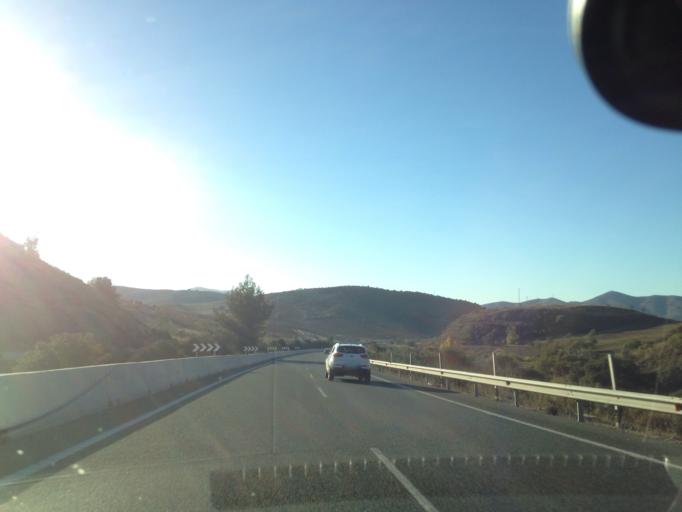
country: ES
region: Andalusia
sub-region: Provincia de Malaga
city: Casabermeja
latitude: 36.9451
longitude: -4.4409
